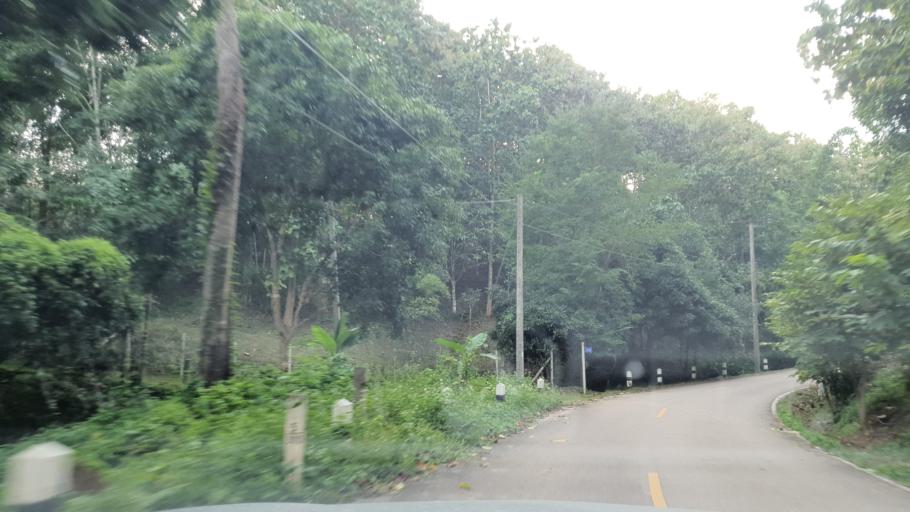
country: TH
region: Chiang Mai
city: Mae On
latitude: 18.8719
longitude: 99.2502
